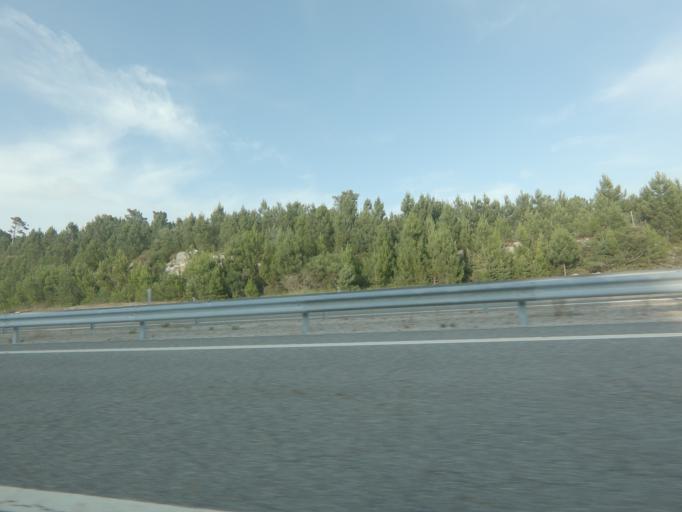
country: PT
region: Vila Real
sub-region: Vila Pouca de Aguiar
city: Vila Pouca de Aguiar
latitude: 41.5011
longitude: -7.6560
